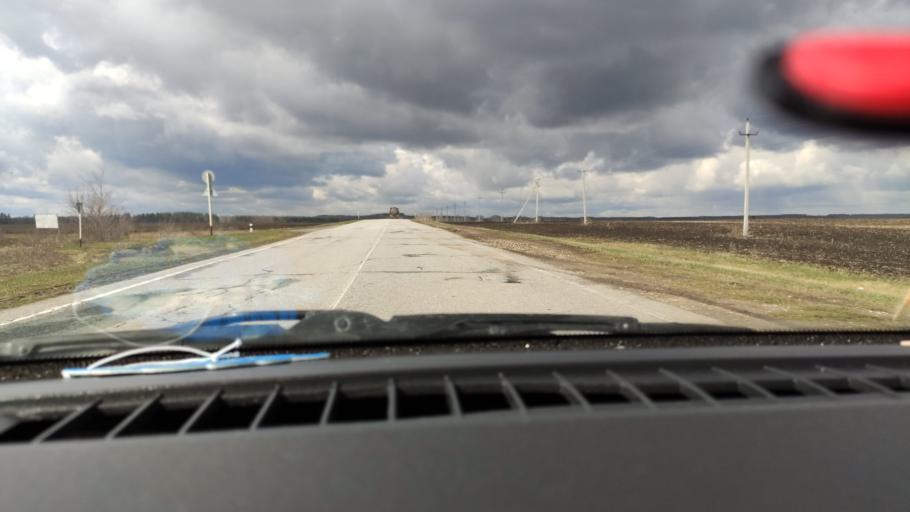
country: RU
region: Samara
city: Yelkhovka
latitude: 53.7594
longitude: 50.2136
